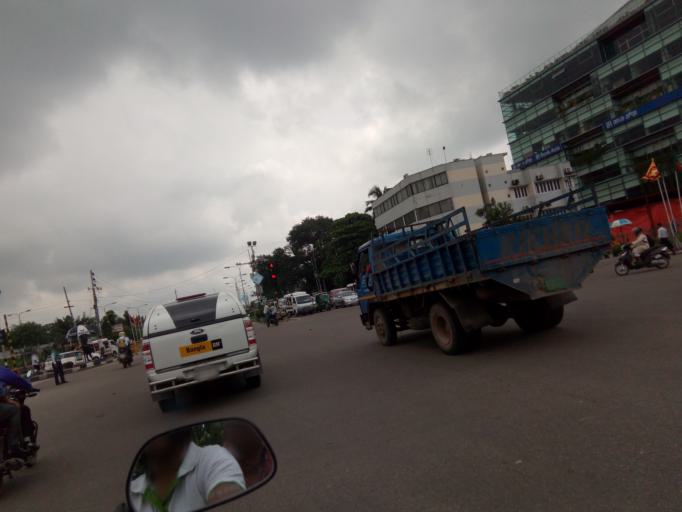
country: BD
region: Dhaka
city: Azimpur
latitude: 23.7642
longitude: 90.3889
